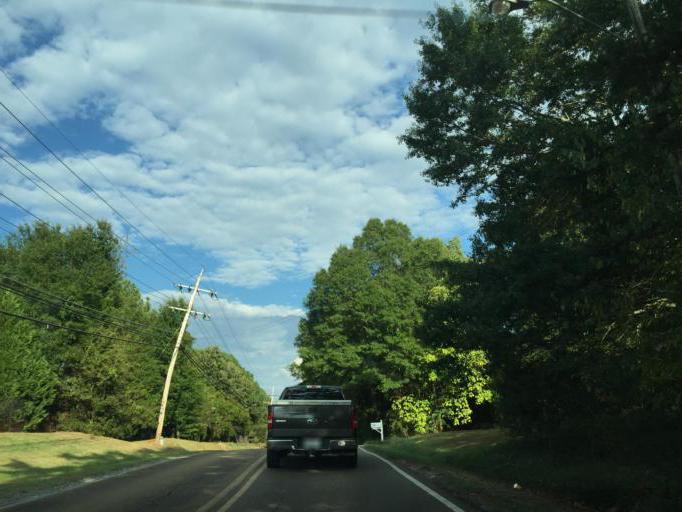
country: US
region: Mississippi
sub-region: Madison County
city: Madison
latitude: 32.4651
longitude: -90.0979
